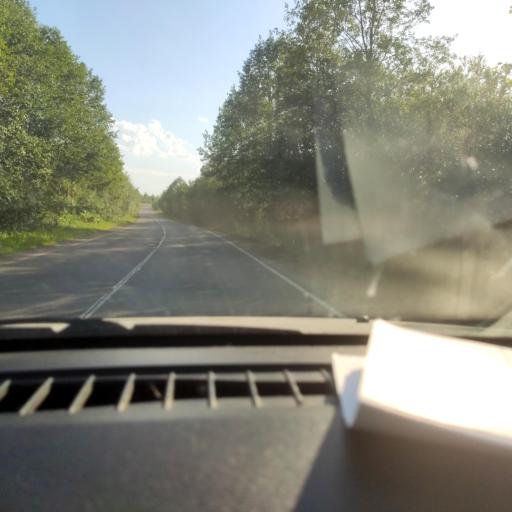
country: RU
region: Perm
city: Krasnokamsk
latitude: 58.1447
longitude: 55.7108
